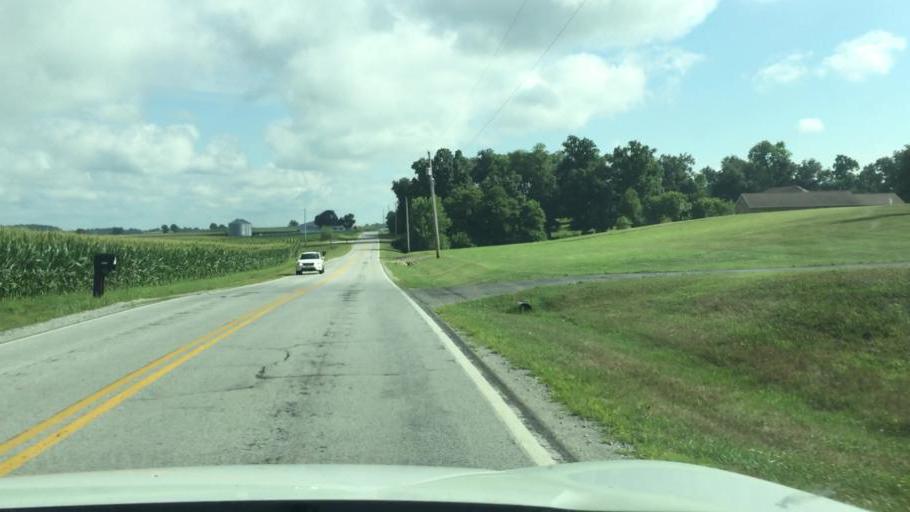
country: US
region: Ohio
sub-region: Clark County
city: Northridge
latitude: 39.9801
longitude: -83.6770
